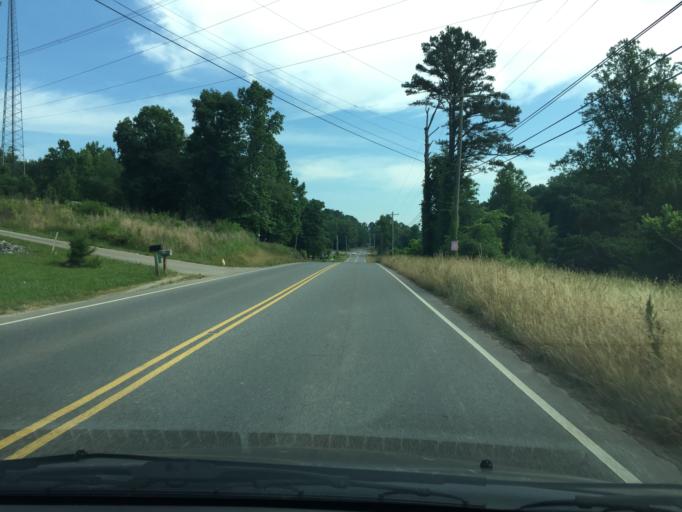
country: US
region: Tennessee
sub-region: Hamilton County
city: Collegedale
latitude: 35.0940
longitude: -85.0082
